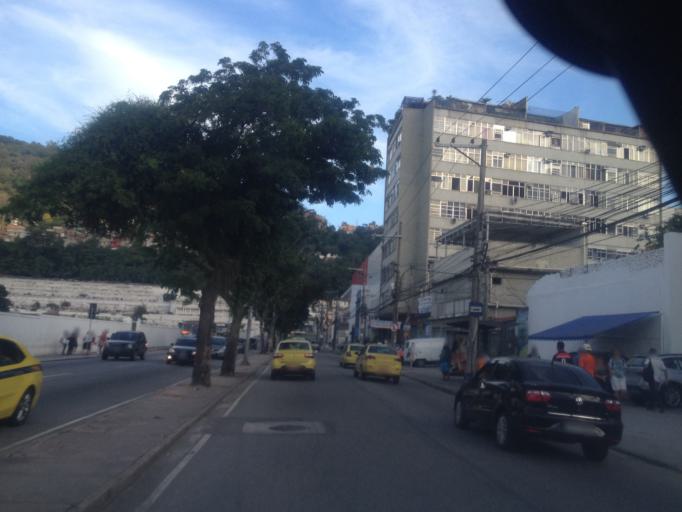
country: BR
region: Rio de Janeiro
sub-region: Rio De Janeiro
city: Rio de Janeiro
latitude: -22.9585
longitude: -43.1913
